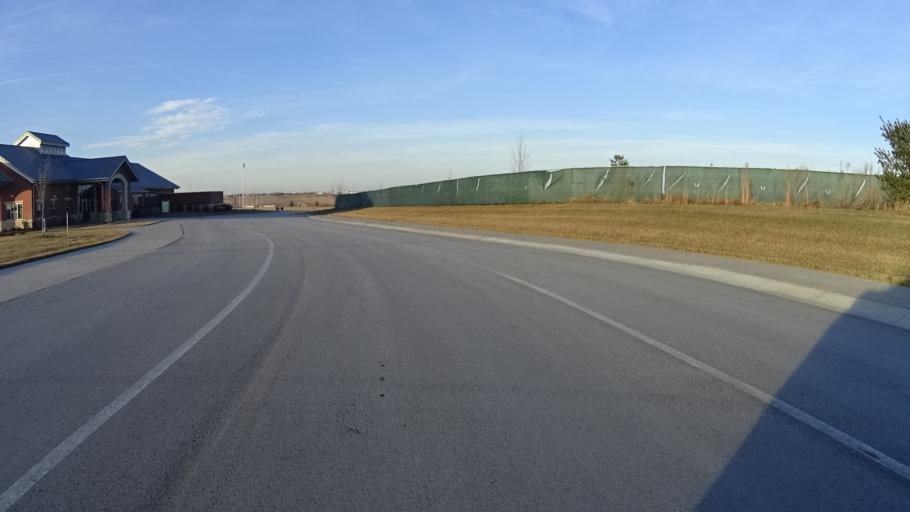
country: US
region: Nebraska
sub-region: Sarpy County
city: Springfield
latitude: 41.1340
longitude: -96.1321
